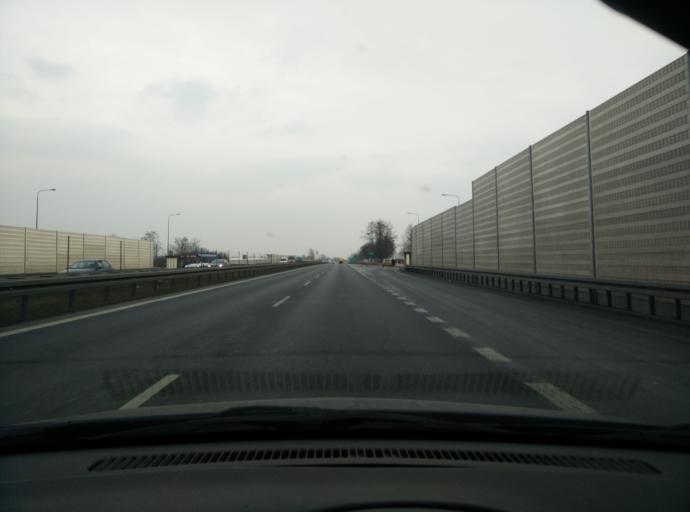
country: PL
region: Greater Poland Voivodeship
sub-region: Powiat poznanski
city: Daszewice
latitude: 52.3362
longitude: 17.0094
